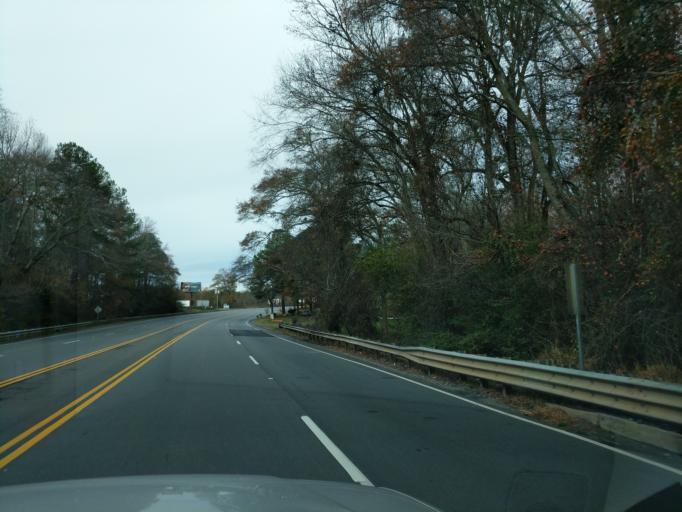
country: US
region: South Carolina
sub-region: Anderson County
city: Pendleton
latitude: 34.6045
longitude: -82.7610
